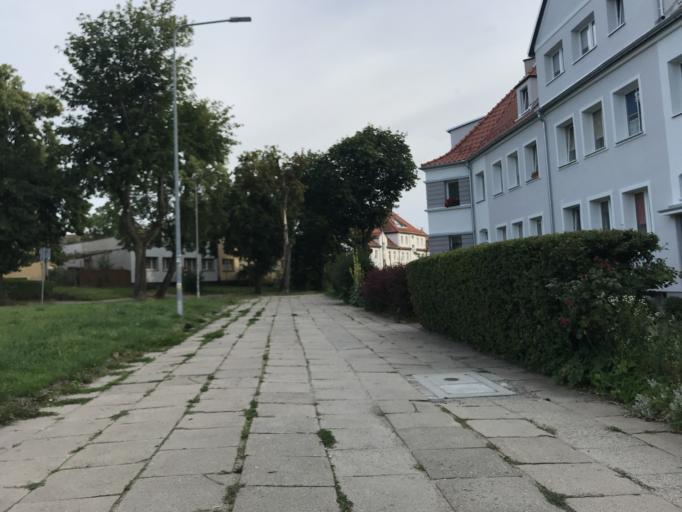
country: PL
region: Warmian-Masurian Voivodeship
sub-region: Powiat elblaski
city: Elblag
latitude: 54.1643
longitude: 19.4219
